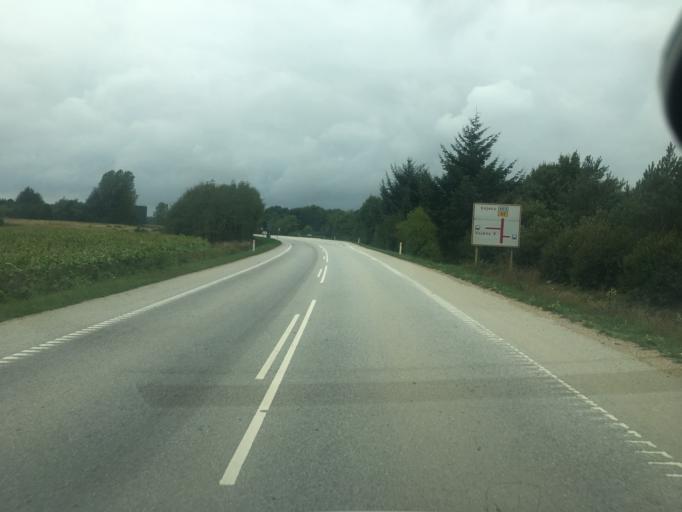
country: DK
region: South Denmark
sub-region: Haderslev Kommune
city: Vojens
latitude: 55.2349
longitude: 9.2972
